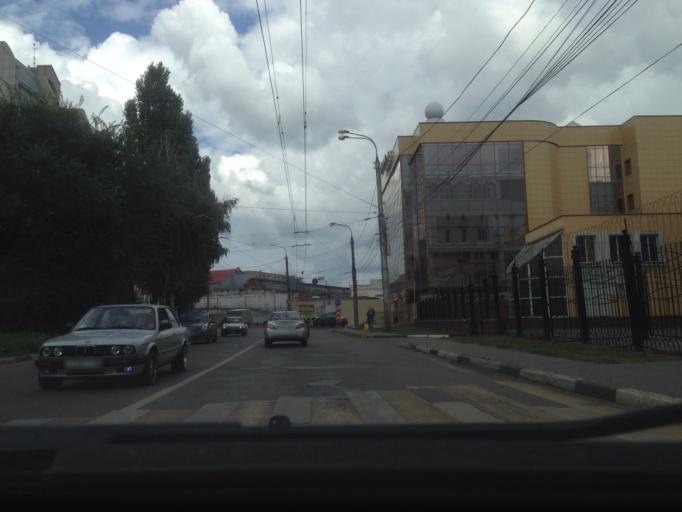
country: RU
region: Voronezj
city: Voronezh
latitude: 51.6740
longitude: 39.1901
